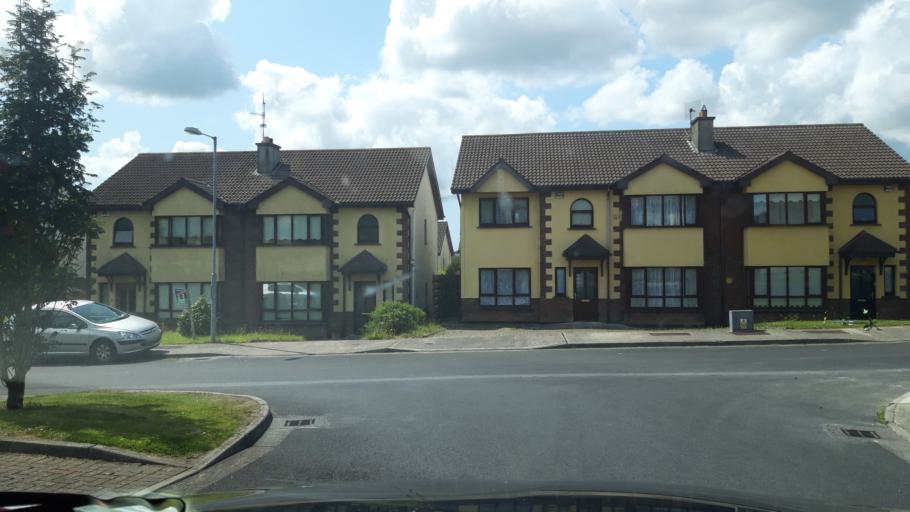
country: IE
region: Munster
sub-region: Waterford
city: Waterford
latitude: 52.2690
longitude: -7.0940
